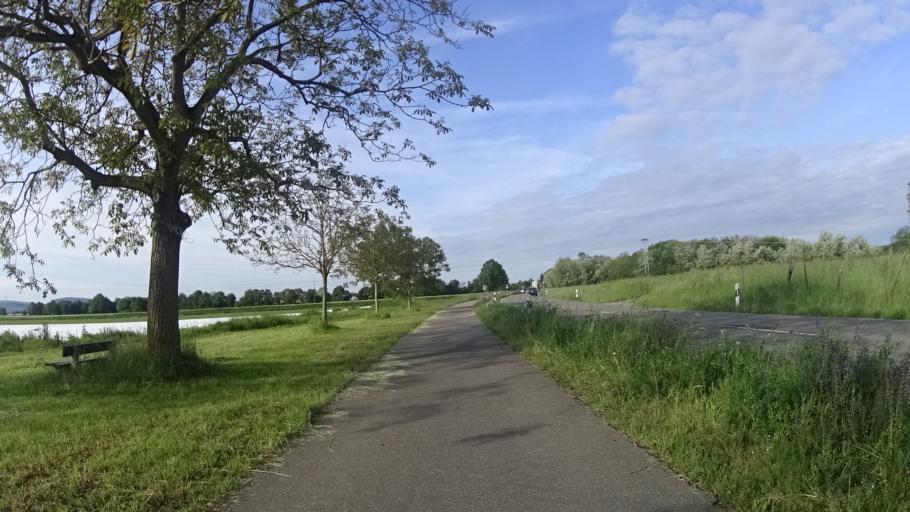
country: DE
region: Baden-Wuerttemberg
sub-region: Freiburg Region
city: Neuenburg am Rhein
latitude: 47.8484
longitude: 7.5829
